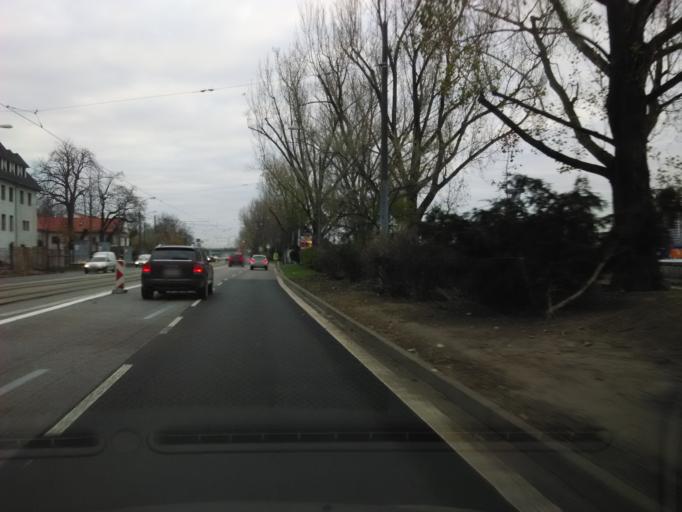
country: SK
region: Bratislavsky
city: Bratislava
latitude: 48.1401
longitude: 17.0963
